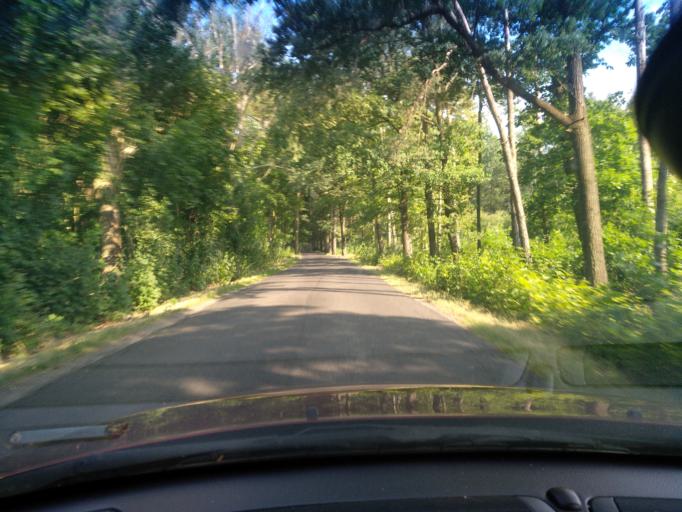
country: PL
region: Lower Silesian Voivodeship
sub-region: Powiat zgorzelecki
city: Lagow
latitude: 51.1230
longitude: 15.0503
